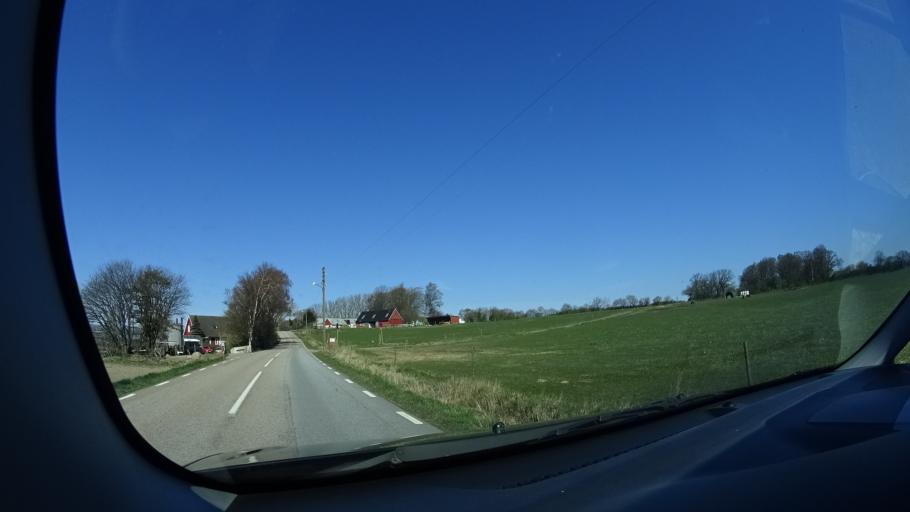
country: SE
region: Skane
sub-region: Hoganas Kommun
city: Hoganas
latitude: 56.2623
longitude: 12.5638
